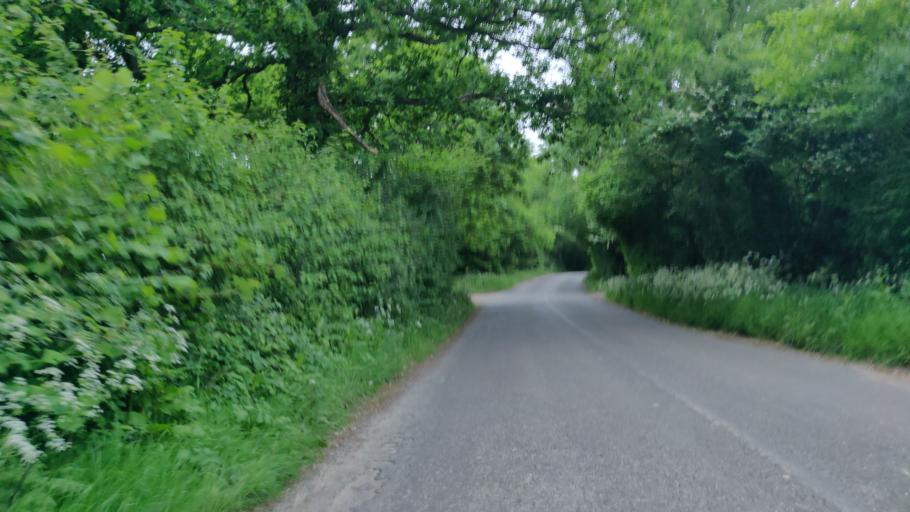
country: GB
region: England
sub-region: West Sussex
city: Partridge Green
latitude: 51.0018
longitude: -0.3077
